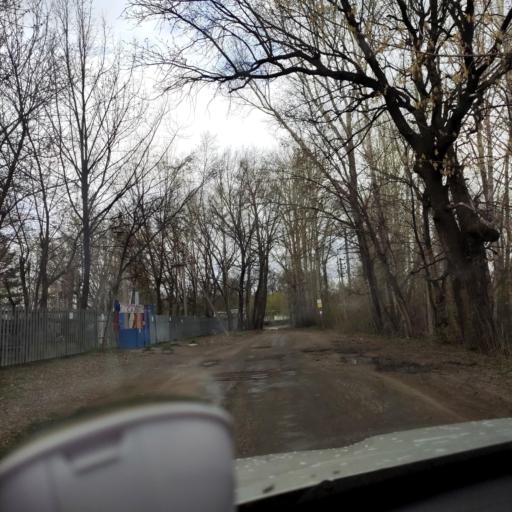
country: RU
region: Samara
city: Novokuybyshevsk
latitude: 53.1405
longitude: 49.9708
